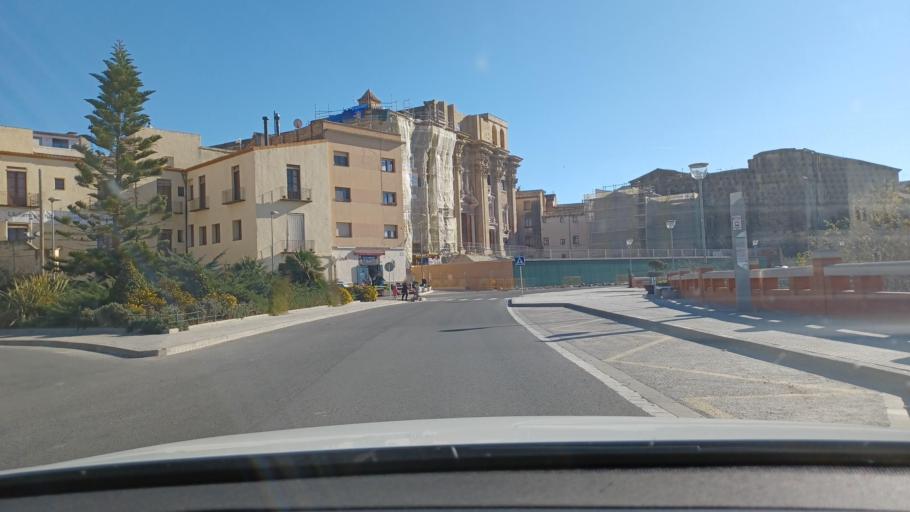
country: ES
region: Catalonia
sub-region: Provincia de Tarragona
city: Tortosa
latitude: 40.8152
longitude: 0.5215
